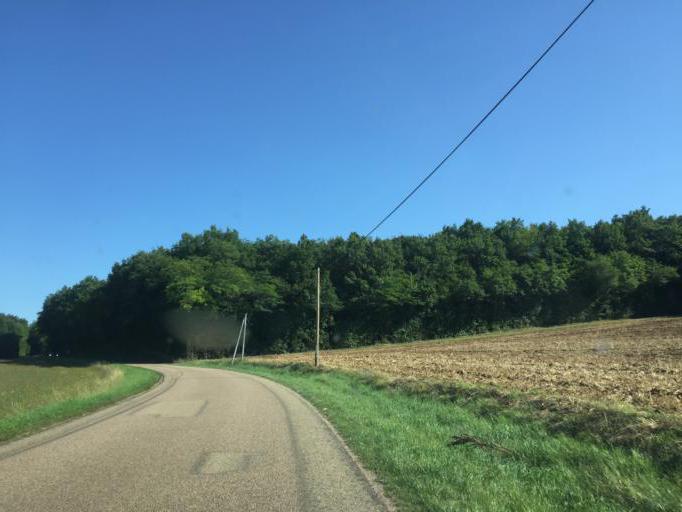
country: FR
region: Bourgogne
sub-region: Departement de l'Yonne
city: Fontenailles
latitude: 47.5531
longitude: 3.3371
